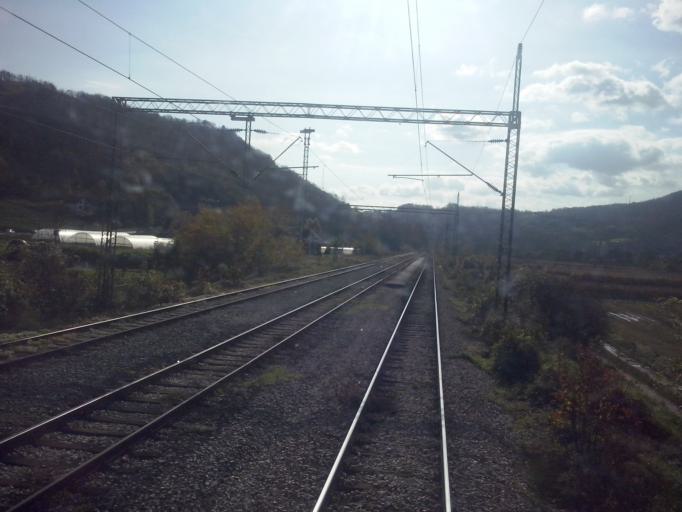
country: RS
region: Central Serbia
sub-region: Zlatiborski Okrug
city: Pozega
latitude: 43.9287
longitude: 19.9893
